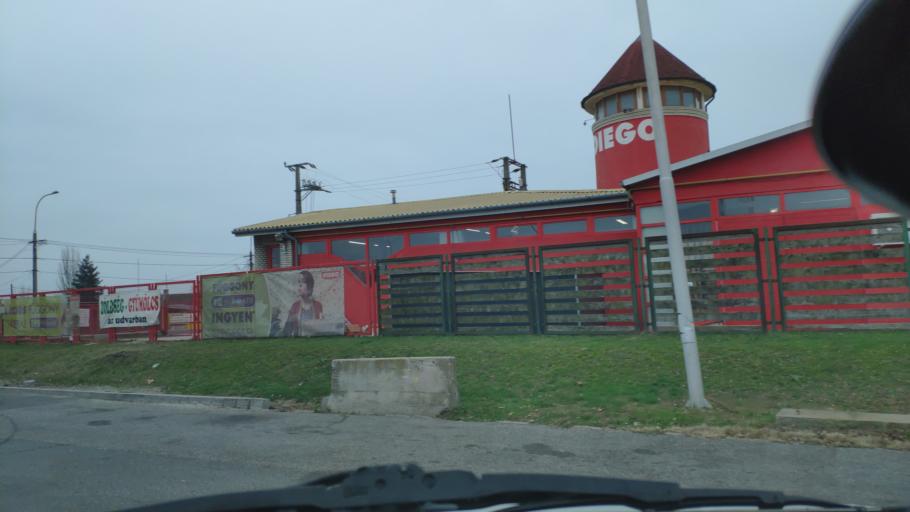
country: HU
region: Budapest
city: Budapest XXII. keruelet
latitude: 47.4012
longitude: 19.0512
